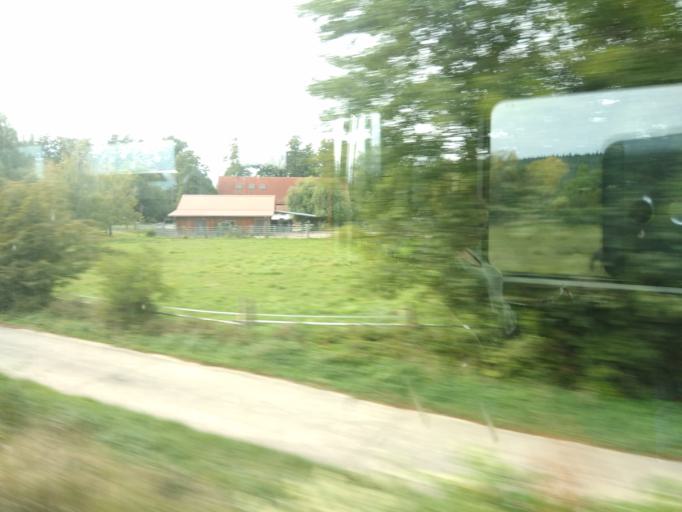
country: DE
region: Baden-Wuerttemberg
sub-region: Karlsruhe Region
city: Weingarten
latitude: 49.0299
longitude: 8.4936
